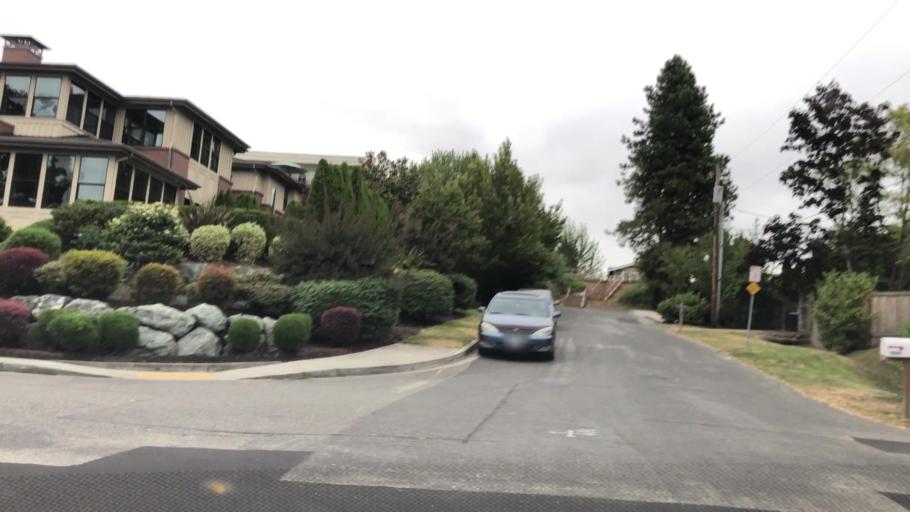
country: US
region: Washington
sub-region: King County
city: Kirkland
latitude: 47.6637
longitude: -122.2021
